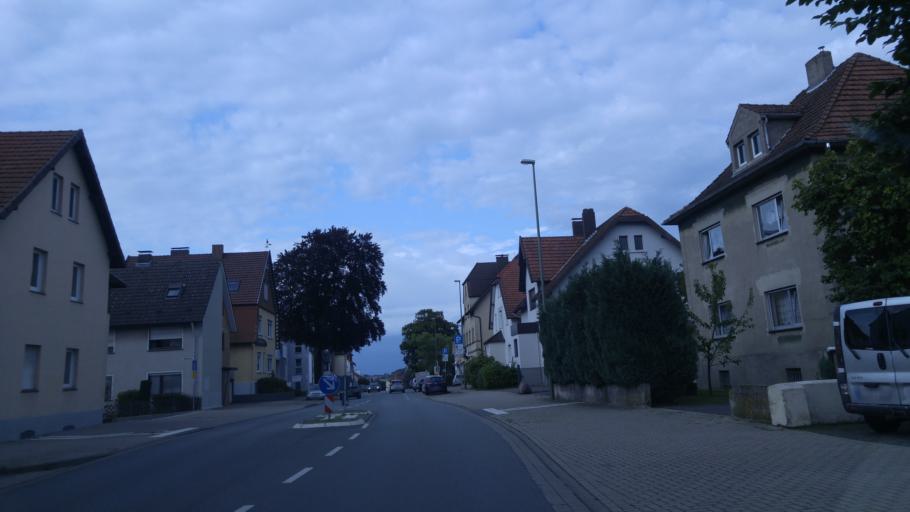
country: DE
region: North Rhine-Westphalia
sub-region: Regierungsbezirk Detmold
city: Bielefeld
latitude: 52.0504
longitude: 8.5463
